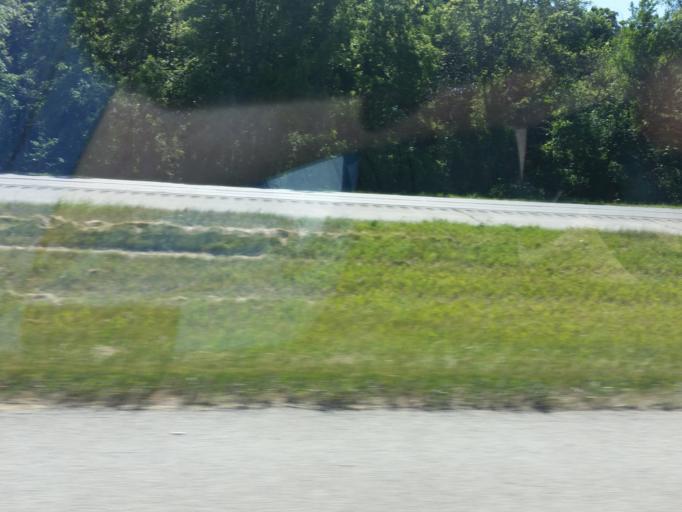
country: US
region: Illinois
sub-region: Winnebago County
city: Roscoe
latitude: 42.4184
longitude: -89.0135
